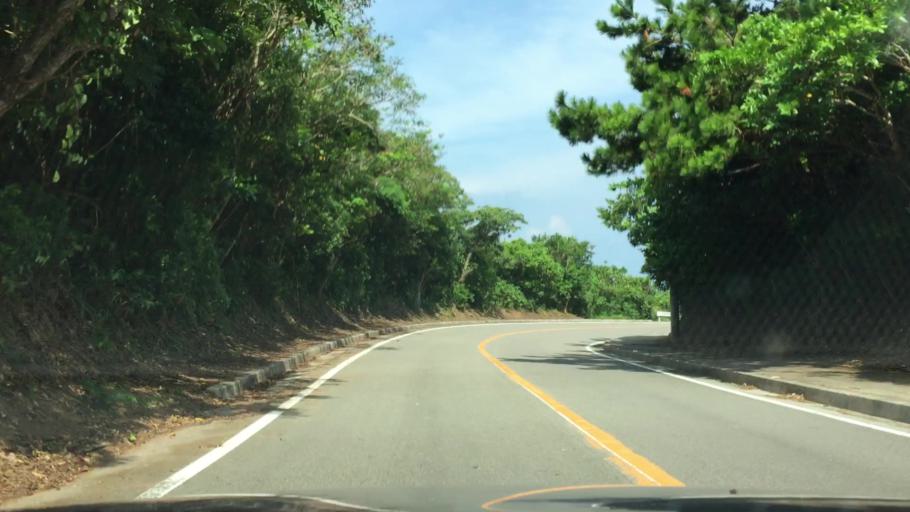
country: JP
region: Okinawa
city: Ishigaki
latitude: 24.5121
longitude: 124.2663
